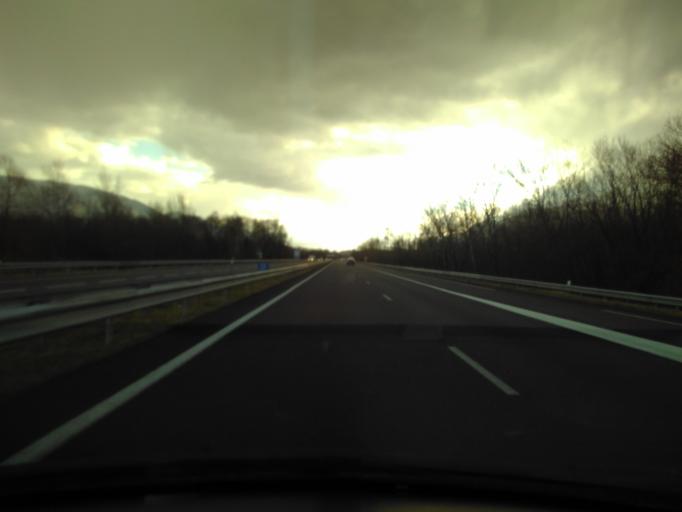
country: FR
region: Rhone-Alpes
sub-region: Departement de la Savoie
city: Les Marches
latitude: 45.4793
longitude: 6.0205
